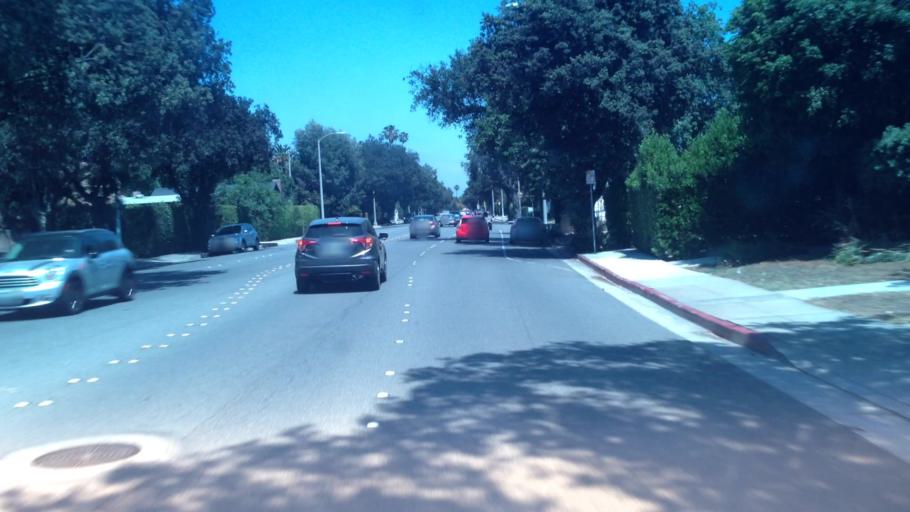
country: US
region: California
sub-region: Los Angeles County
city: East Pasadena
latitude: 34.1419
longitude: -118.1128
